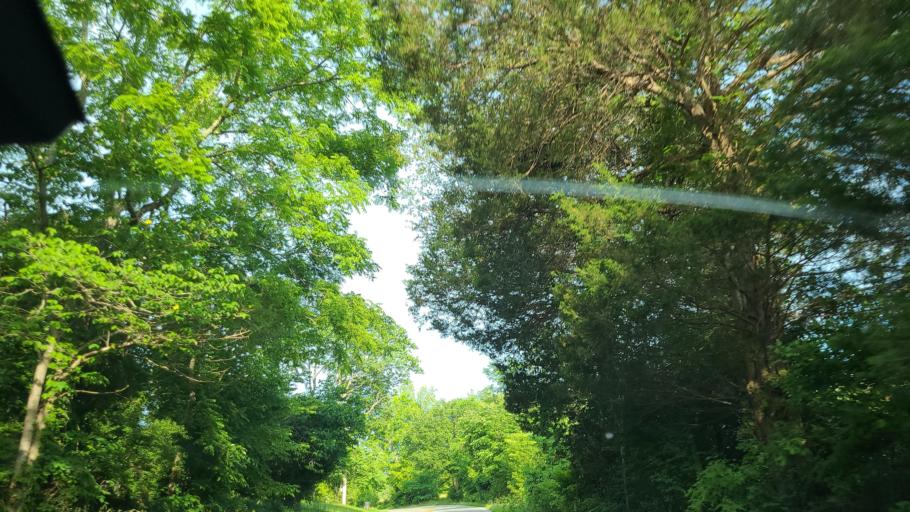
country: US
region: Kentucky
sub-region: Whitley County
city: Corbin
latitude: 36.8824
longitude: -84.2083
